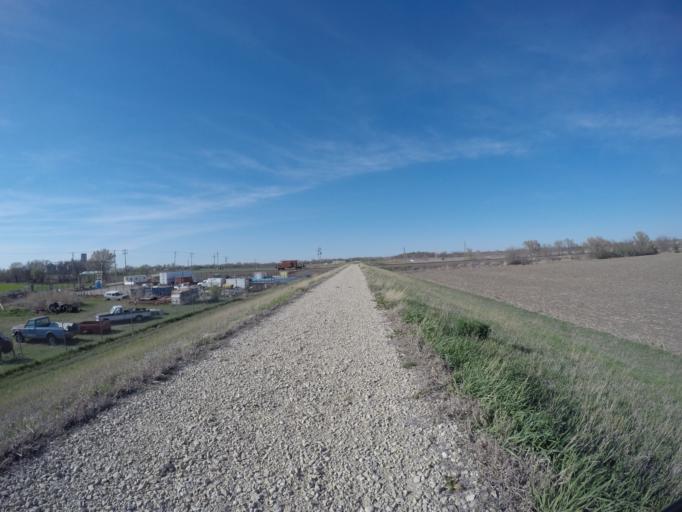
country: US
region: Kansas
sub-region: Saline County
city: Salina
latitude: 38.8513
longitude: -97.5748
